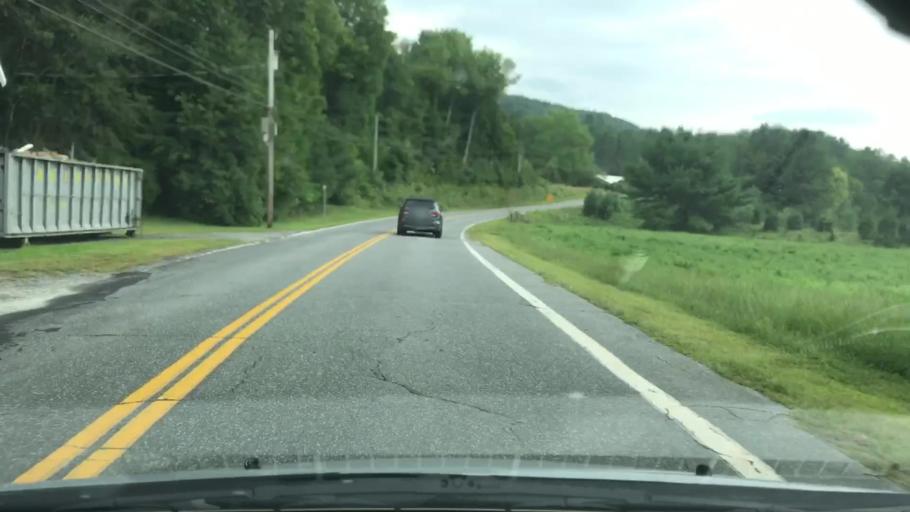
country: US
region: New Hampshire
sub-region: Grafton County
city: Orford
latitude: 43.9245
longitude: -72.1137
